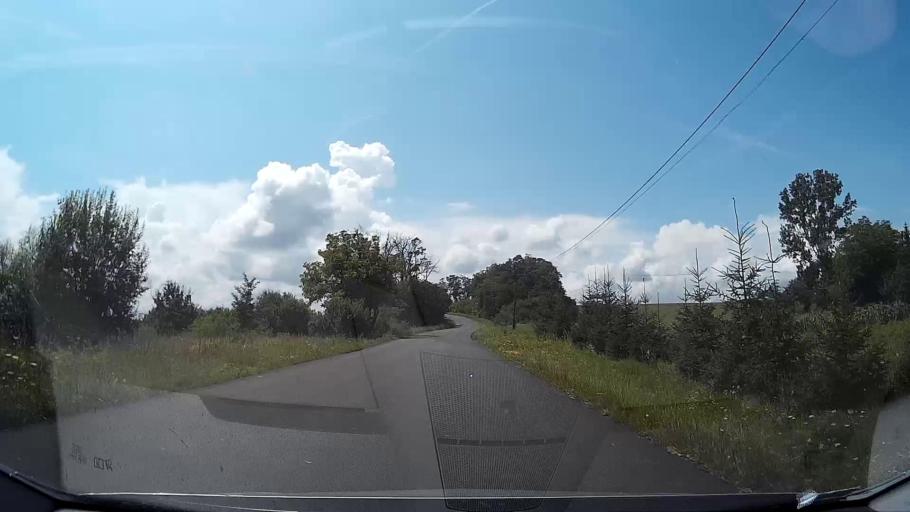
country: SK
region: Banskobystricky
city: Fil'akovo
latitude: 48.3151
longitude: 19.8076
